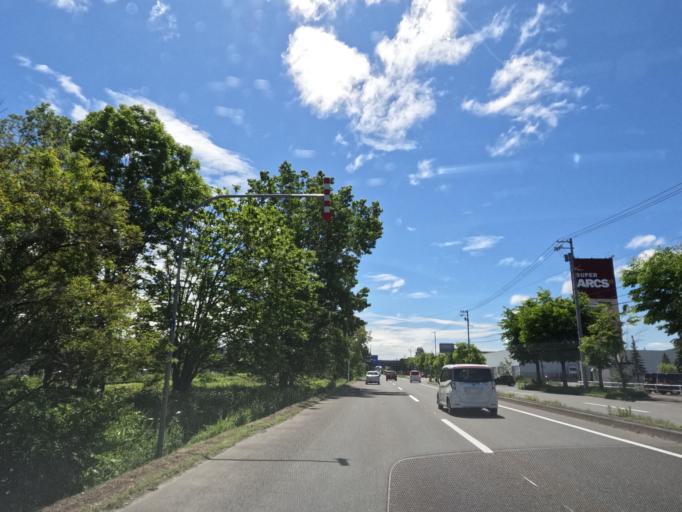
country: JP
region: Hokkaido
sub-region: Asahikawa-shi
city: Asahikawa
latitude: 43.7294
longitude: 142.3664
